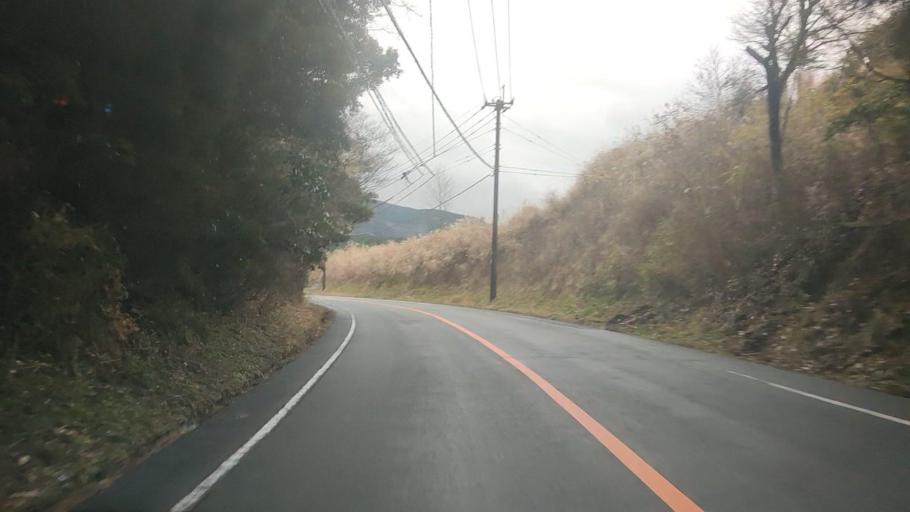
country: JP
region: Kumamoto
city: Aso
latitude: 32.8912
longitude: 131.0210
